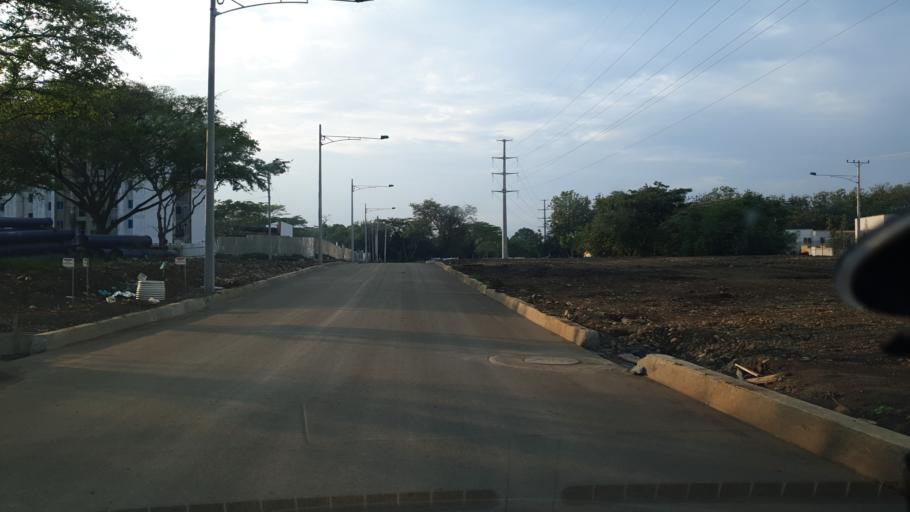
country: CO
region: Valle del Cauca
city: Jamundi
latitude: 3.3462
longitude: -76.5152
